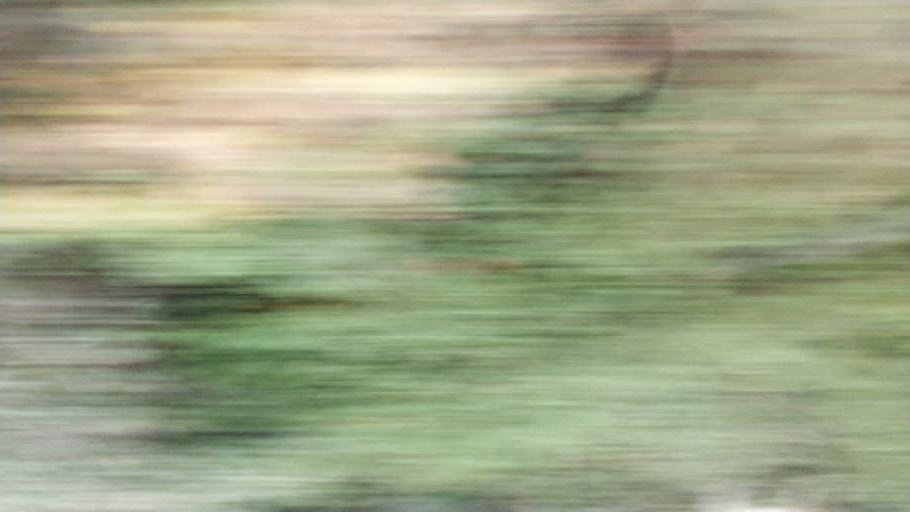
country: GB
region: England
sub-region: Borough of Bolton
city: Westhoughton
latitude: 53.5400
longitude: -2.5182
